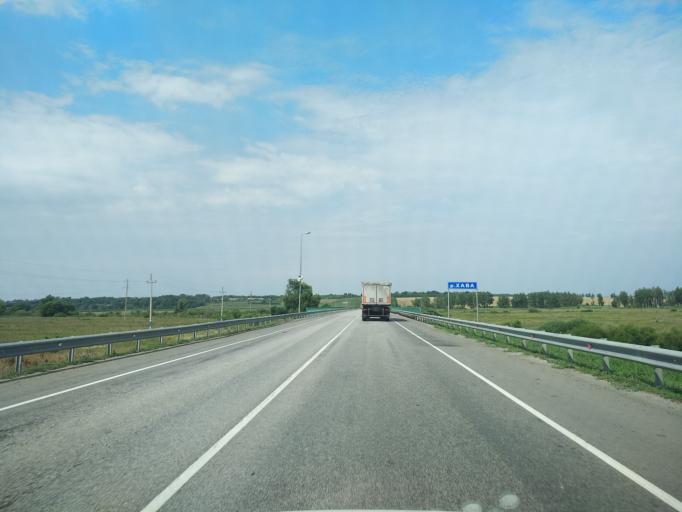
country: RU
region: Voronezj
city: Orlovo
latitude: 51.6757
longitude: 39.7384
